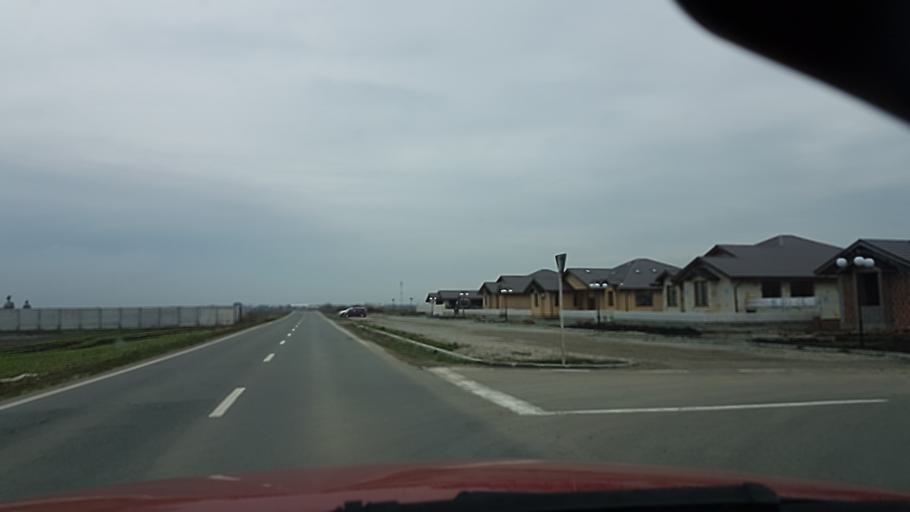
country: RO
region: Ilfov
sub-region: Comuna Balotesti
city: Balotesti
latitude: 44.6061
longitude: 26.1303
